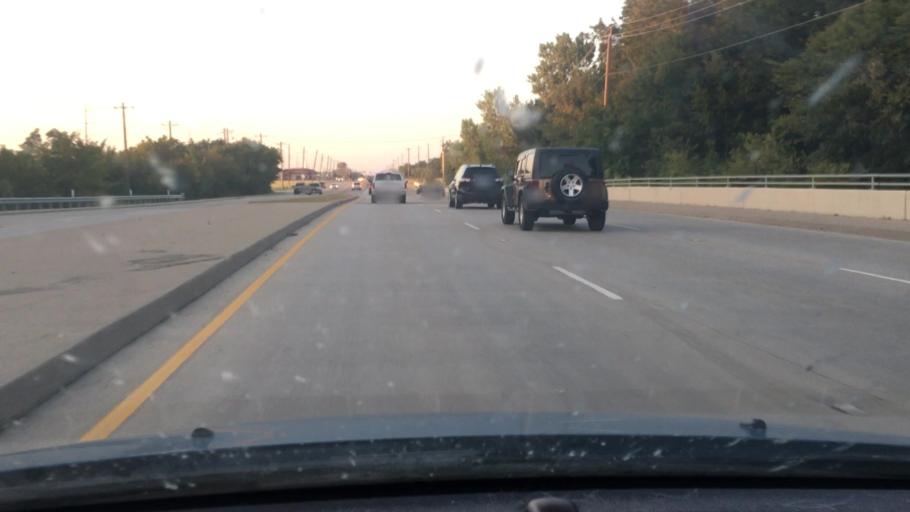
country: US
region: Texas
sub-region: Denton County
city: Denton
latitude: 33.2067
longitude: -97.0909
